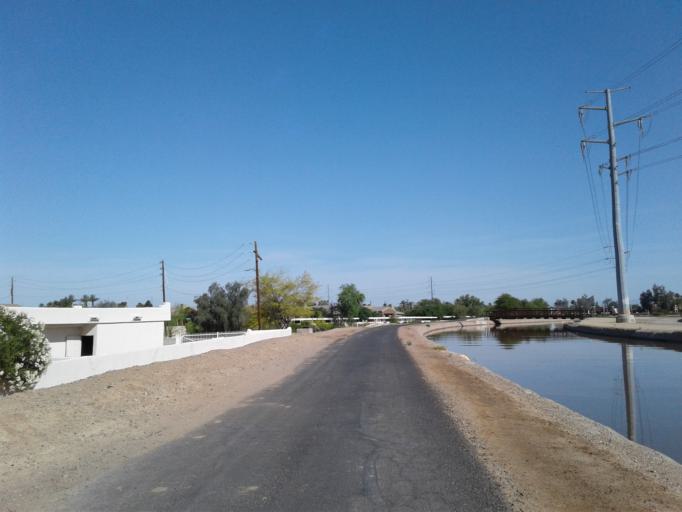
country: US
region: Arizona
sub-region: Maricopa County
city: Glendale
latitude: 33.5922
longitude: -112.1660
